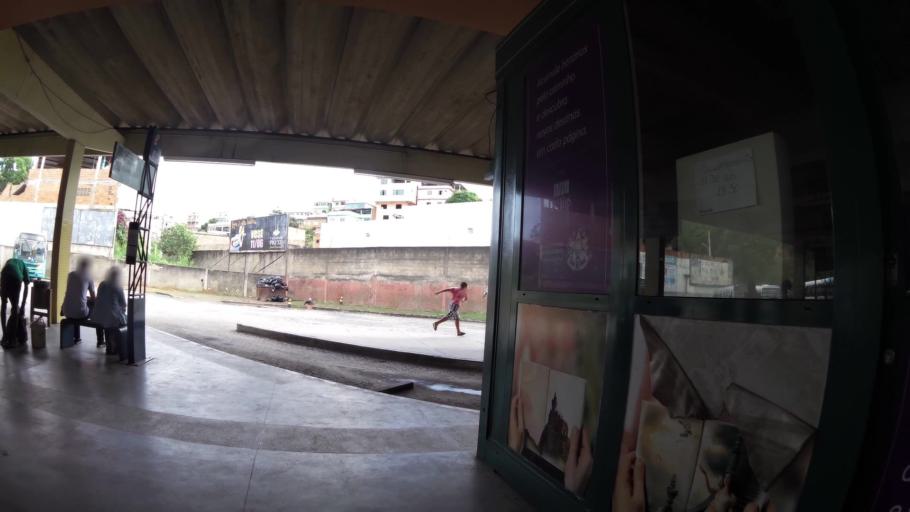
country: BR
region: Espirito Santo
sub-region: Vitoria
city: Vitoria
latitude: -20.3305
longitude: -40.3781
